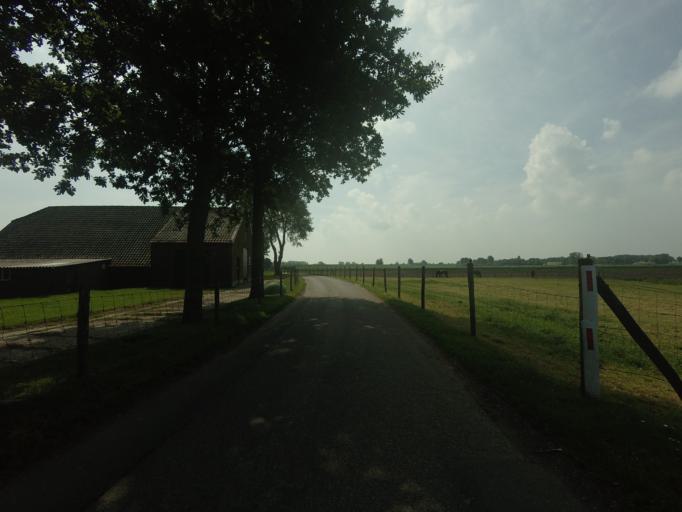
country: NL
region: Utrecht
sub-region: Gemeente IJsselstein
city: IJsselstein
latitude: 51.9986
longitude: 5.0611
